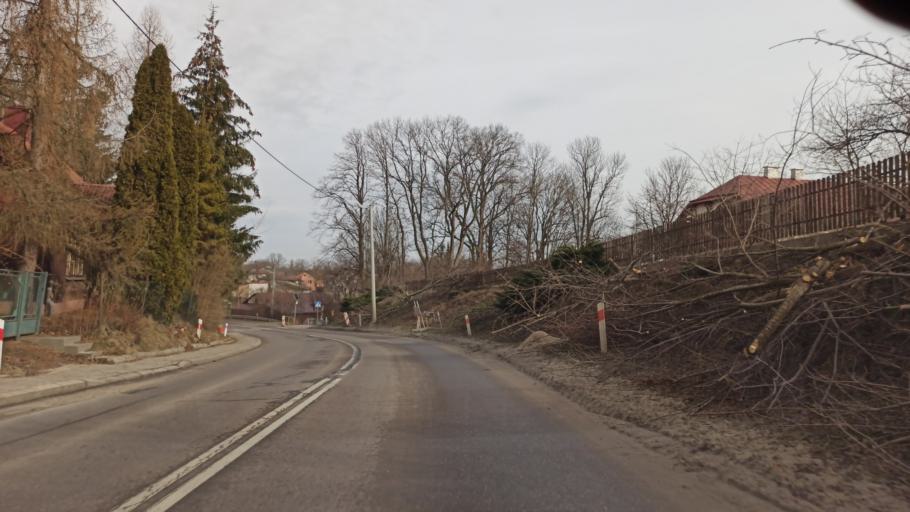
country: PL
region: Lublin Voivodeship
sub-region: Powiat bilgorajski
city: Tarnogrod
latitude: 50.3634
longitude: 22.7435
